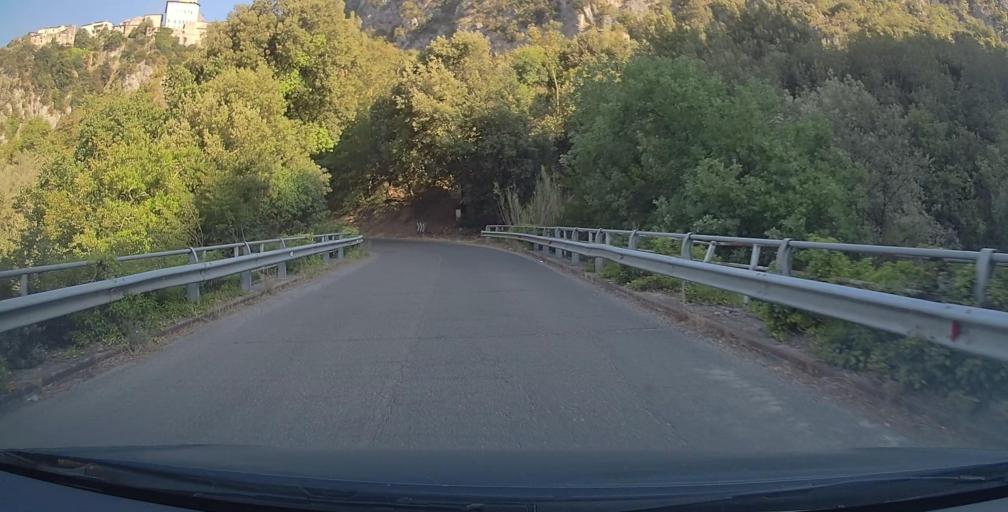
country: IT
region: Umbria
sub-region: Provincia di Terni
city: Calvi dell'Umbria
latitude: 42.4002
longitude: 12.5723
